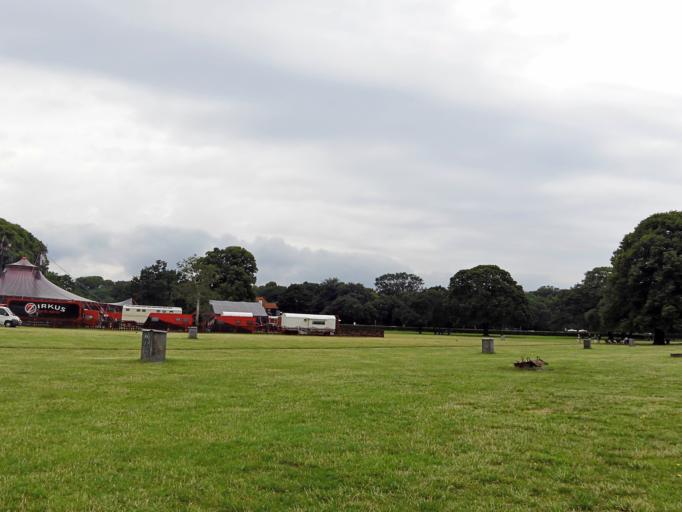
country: DK
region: Capital Region
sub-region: Gentofte Kommune
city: Charlottenlund
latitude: 55.7478
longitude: 12.5895
